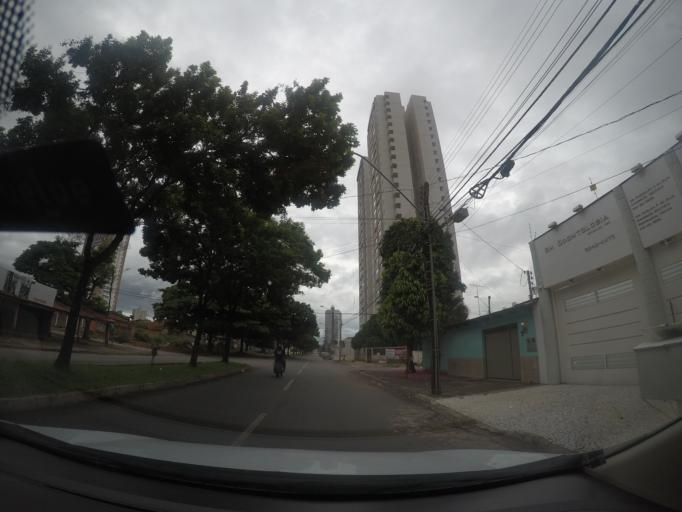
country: BR
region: Goias
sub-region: Goiania
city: Goiania
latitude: -16.7317
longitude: -49.2765
